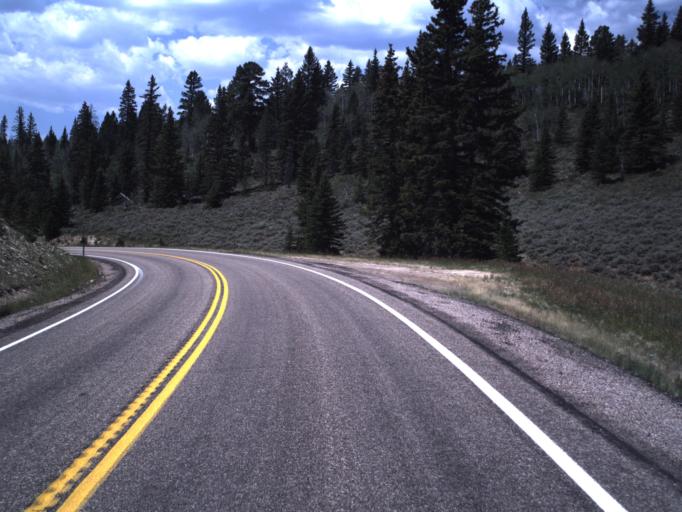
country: US
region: Utah
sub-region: Uintah County
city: Maeser
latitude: 40.7156
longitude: -109.4892
